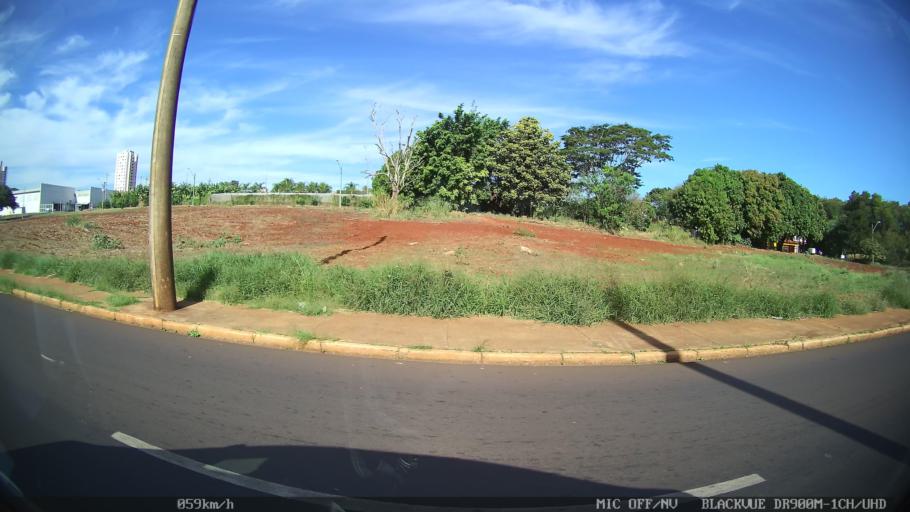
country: BR
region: Sao Paulo
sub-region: Araraquara
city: Araraquara
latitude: -21.8083
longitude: -48.1745
